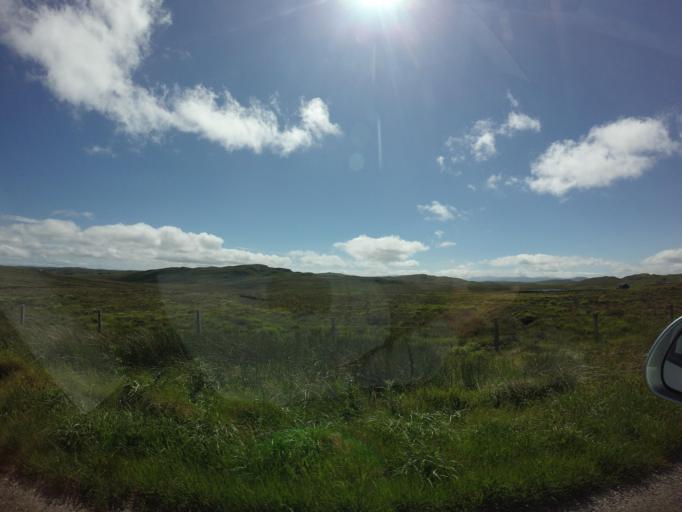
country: GB
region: Scotland
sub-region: Eilean Siar
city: Stornoway
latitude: 58.1578
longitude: -6.5194
